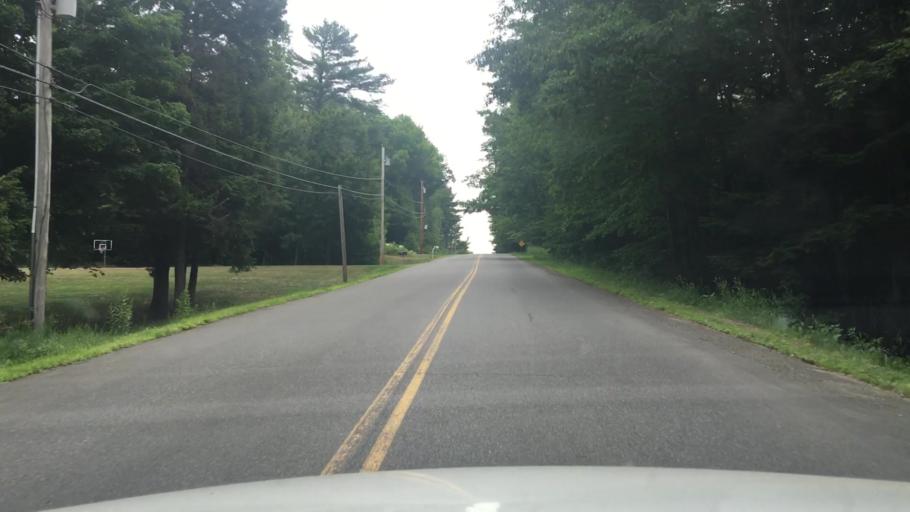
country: US
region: Maine
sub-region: Kennebec County
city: Benton
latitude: 44.5811
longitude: -69.5103
